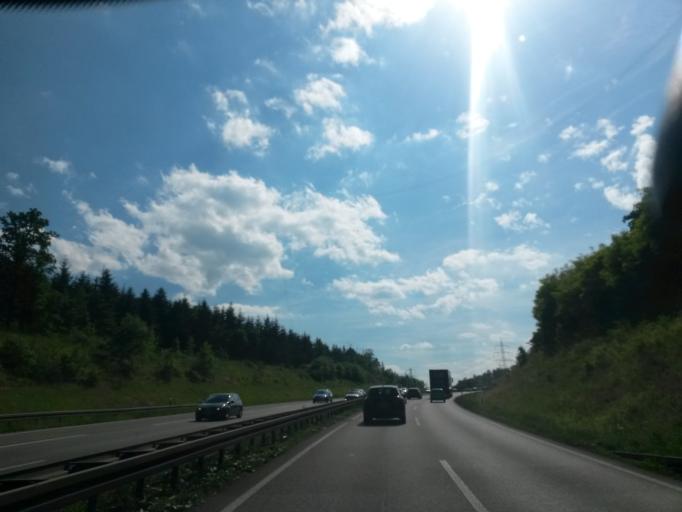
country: DE
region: Baden-Wuerttemberg
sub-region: Regierungsbezirk Stuttgart
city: Rutesheim
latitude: 48.7832
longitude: 8.9776
